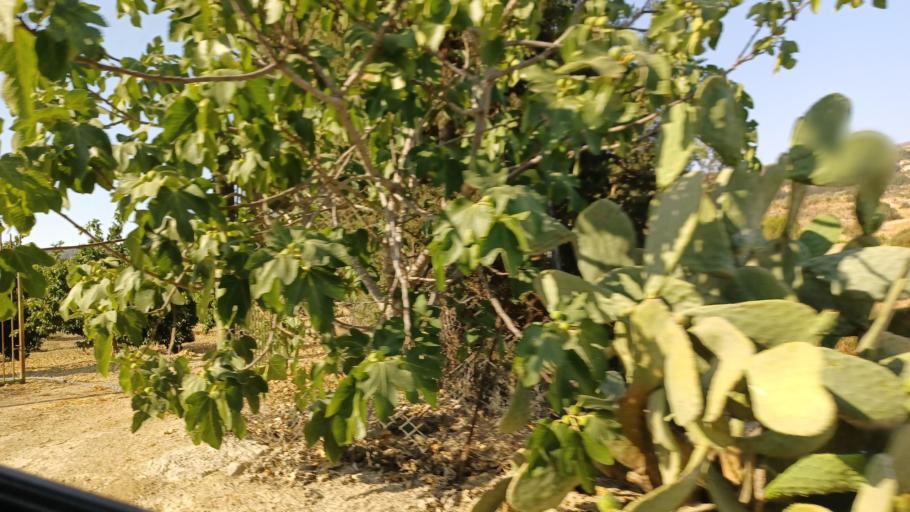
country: CY
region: Pafos
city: Tala
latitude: 34.9107
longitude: 32.4831
